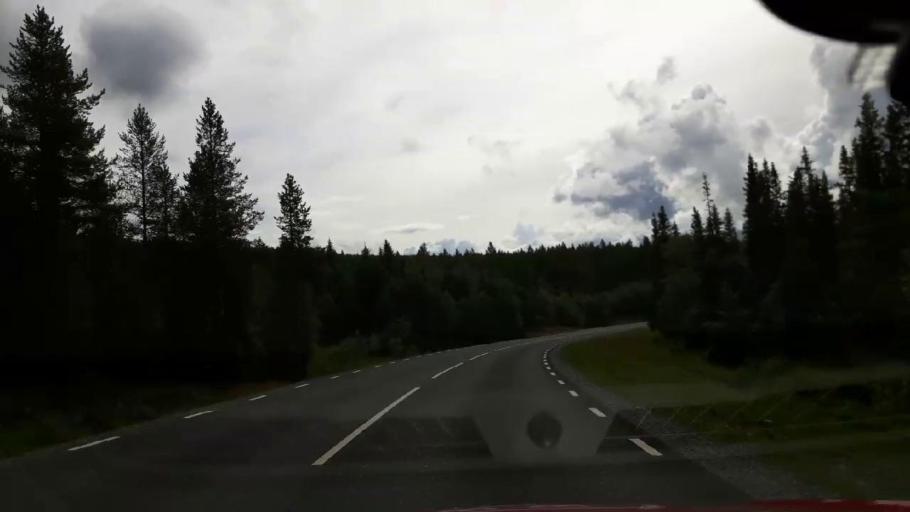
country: NO
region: Nord-Trondelag
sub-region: Lierne
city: Sandvika
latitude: 64.6342
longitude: 14.1416
